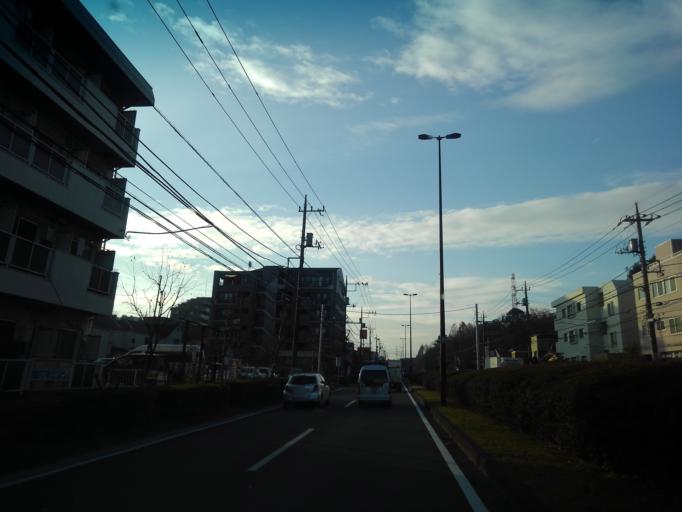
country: JP
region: Tokyo
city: Hino
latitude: 35.6288
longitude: 139.4424
